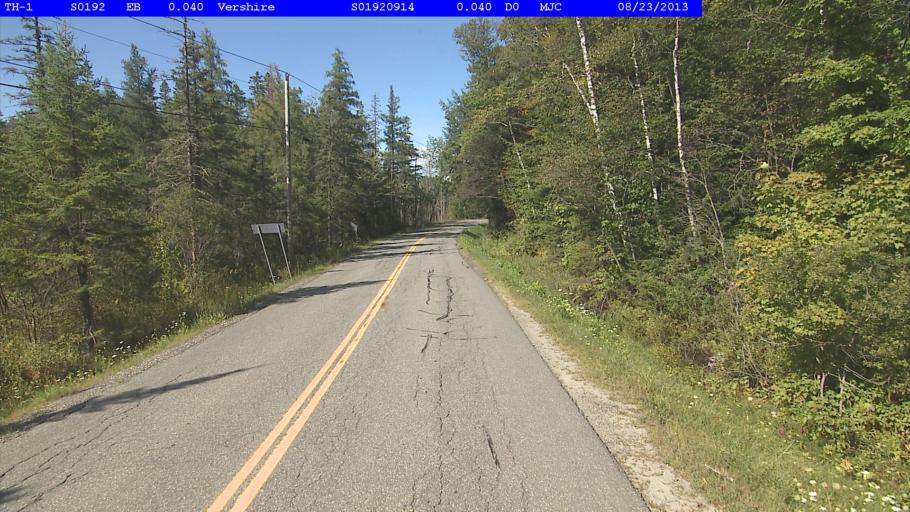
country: US
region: Vermont
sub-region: Orange County
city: Chelsea
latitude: 43.9882
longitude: -72.3691
